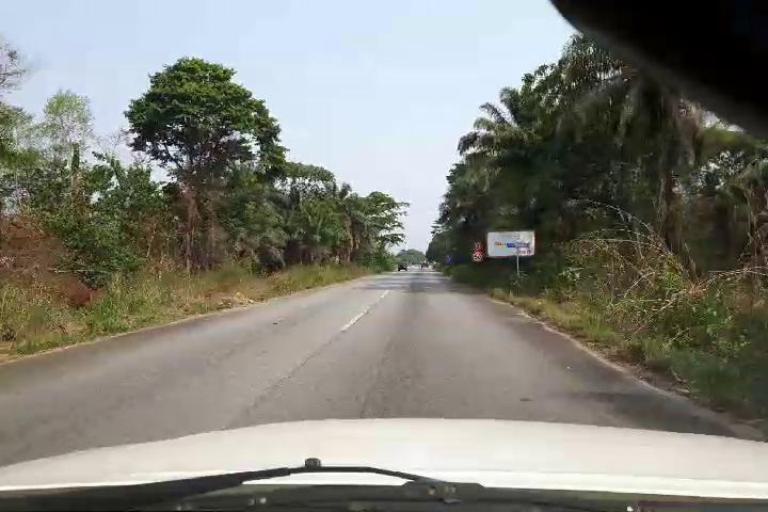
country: SL
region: Southern Province
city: Baiima
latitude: 8.1361
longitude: -11.8890
